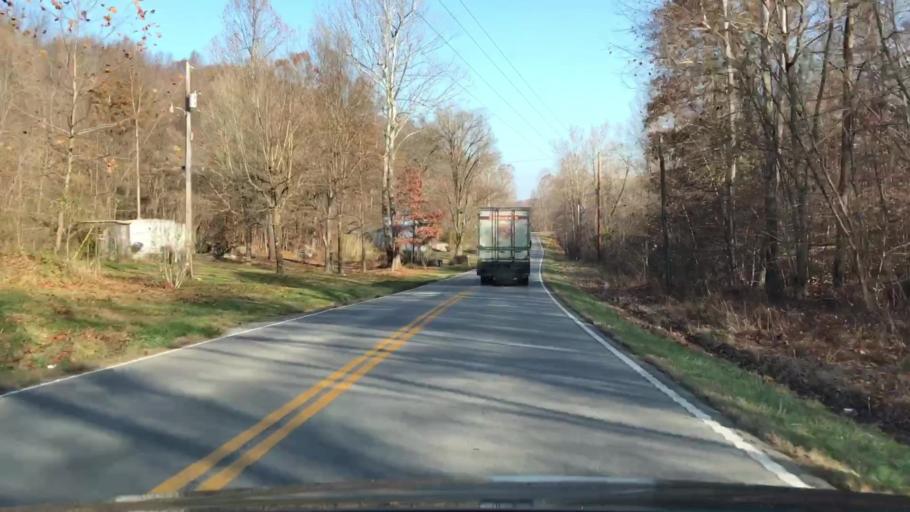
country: US
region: Kentucky
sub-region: Grayson County
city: Leitchfield
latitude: 37.4210
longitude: -86.2786
